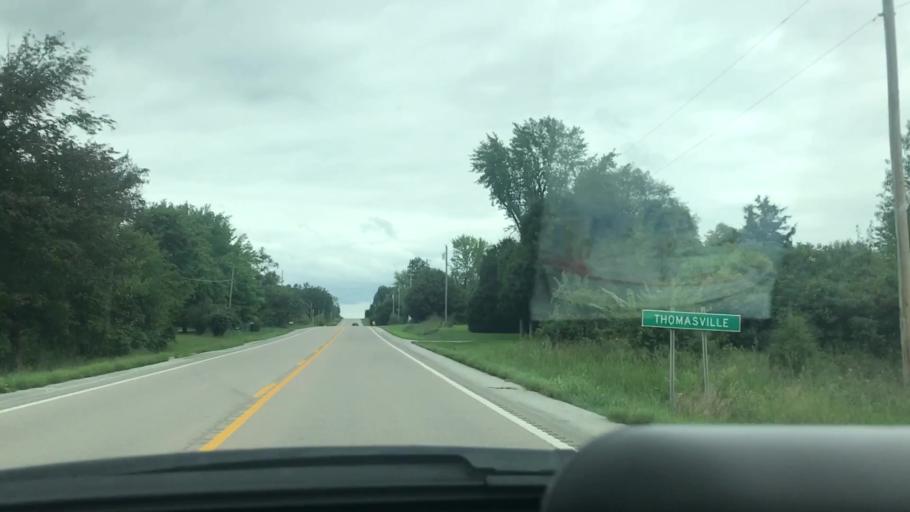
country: US
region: Missouri
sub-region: Dallas County
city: Buffalo
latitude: 37.6982
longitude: -93.1051
